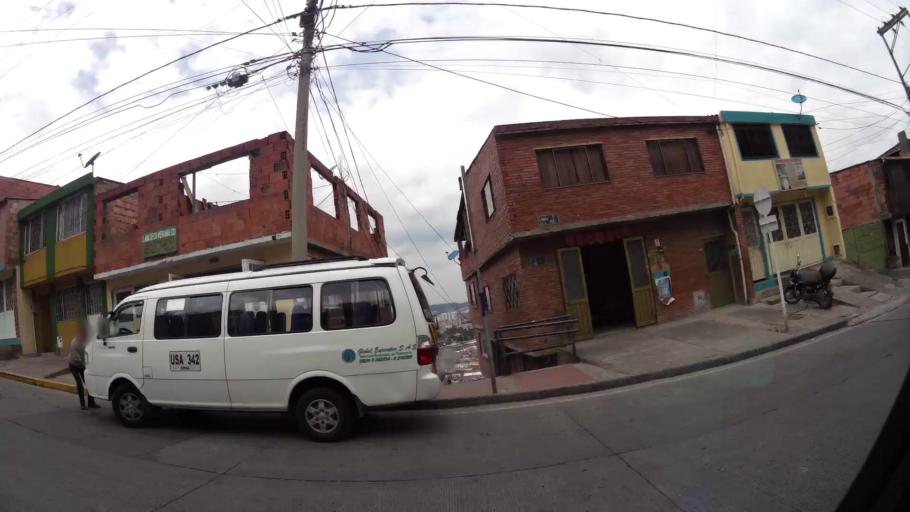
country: CO
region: Cundinamarca
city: La Calera
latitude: 4.7651
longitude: -74.0259
